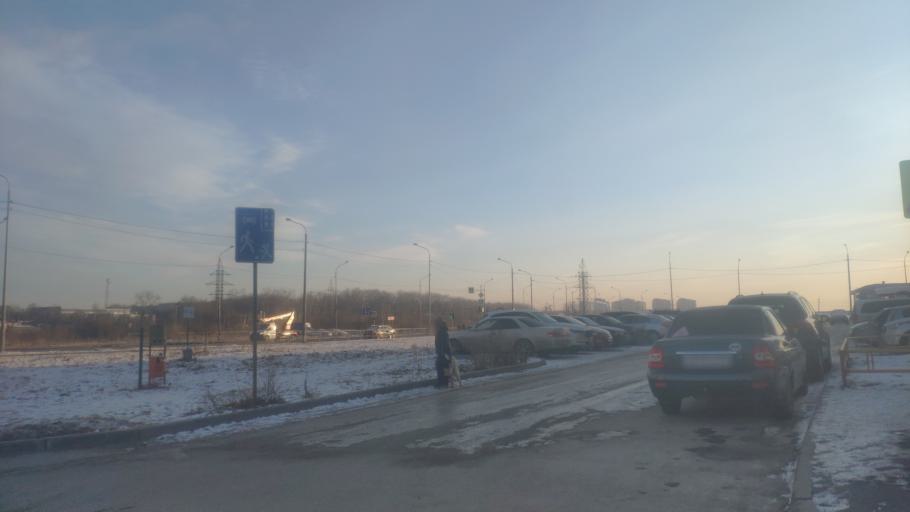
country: RU
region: Tjumen
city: Tyumen
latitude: 57.1780
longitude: 65.5676
